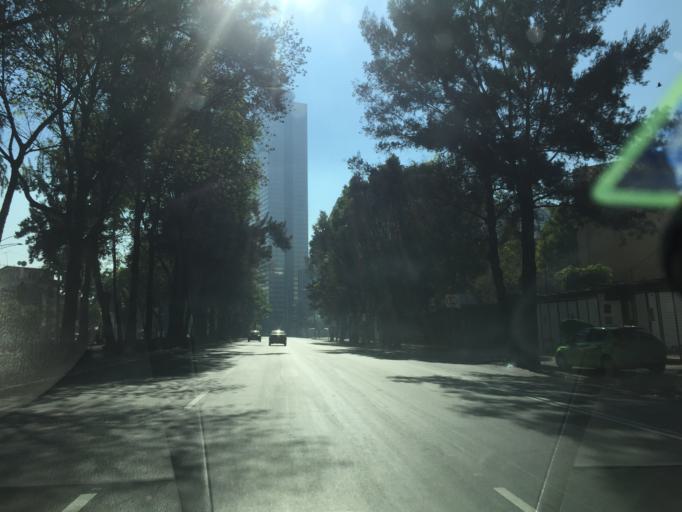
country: MX
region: Mexico City
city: Miguel Hidalgo
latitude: 19.4428
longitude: -99.1780
